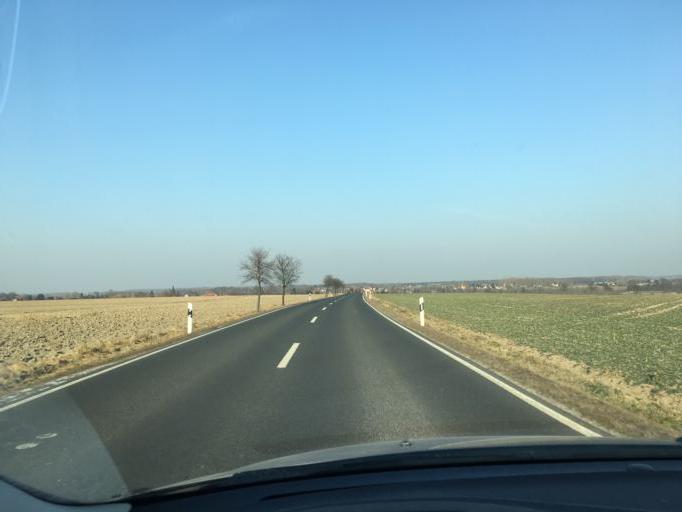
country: DE
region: Saxony
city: Kitzscher
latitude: 51.1144
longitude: 12.5839
